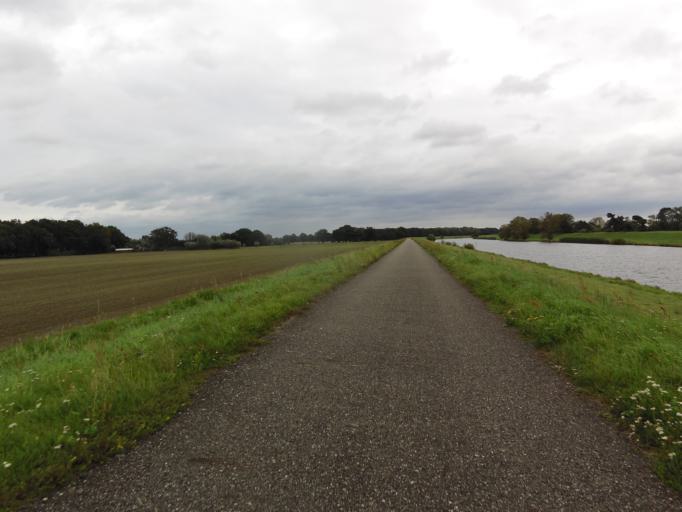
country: DE
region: Brandenburg
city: Ruhstadt
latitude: 52.8948
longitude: 11.9163
